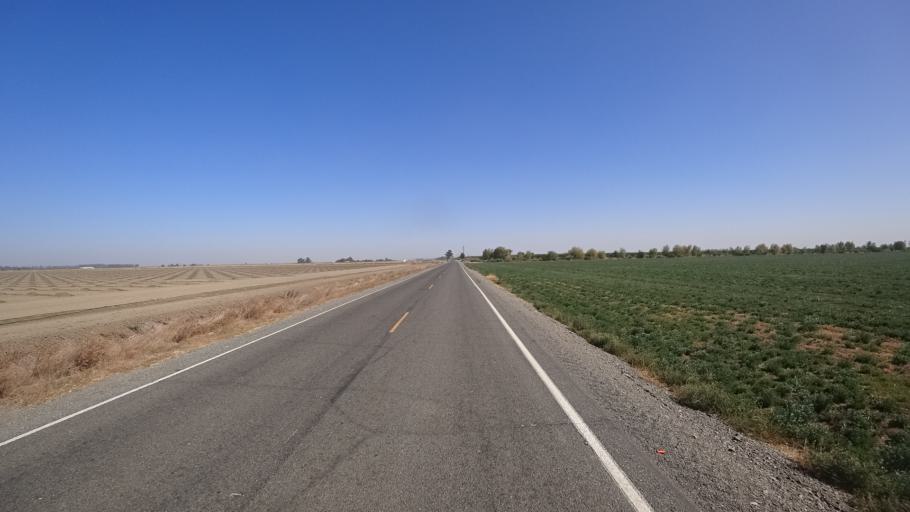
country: US
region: California
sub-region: Yolo County
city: Winters
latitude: 38.5907
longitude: -121.8985
